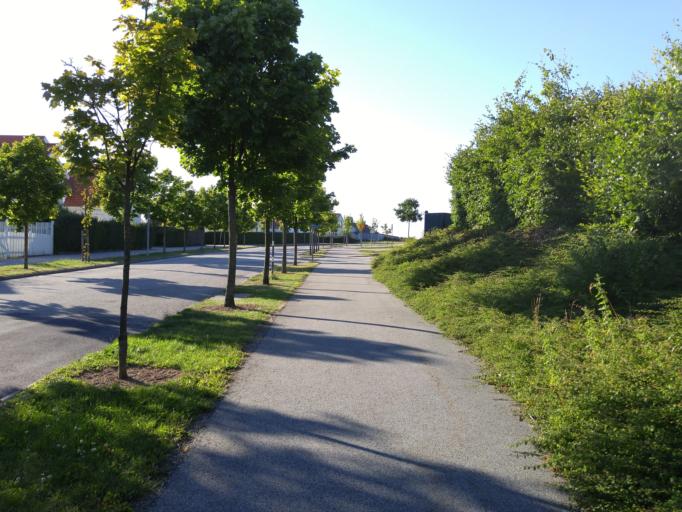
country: SE
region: Skane
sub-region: Lunds Kommun
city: Lund
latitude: 55.7306
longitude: 13.1938
